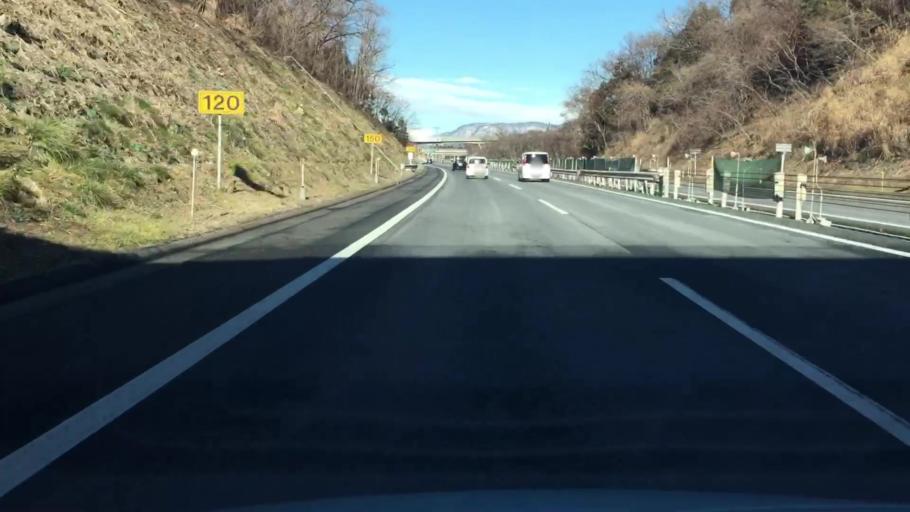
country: JP
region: Gunma
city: Numata
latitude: 36.5940
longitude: 139.0659
